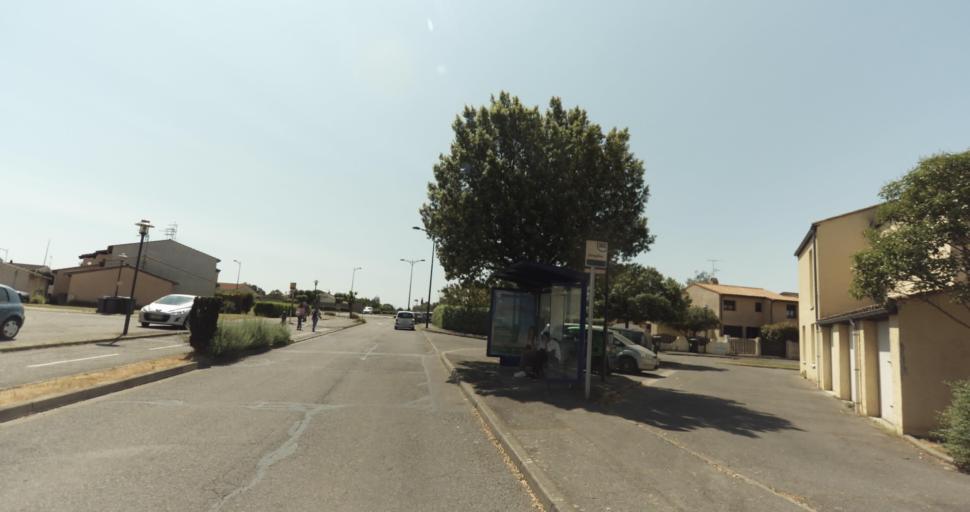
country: FR
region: Midi-Pyrenees
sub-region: Departement de la Haute-Garonne
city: Plaisance-du-Touch
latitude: 43.5617
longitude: 1.3047
